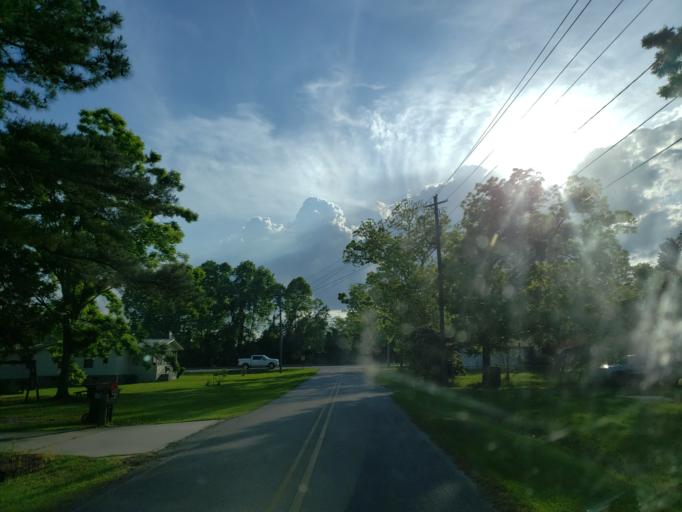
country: US
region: Georgia
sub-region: Lowndes County
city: Hahira
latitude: 31.0446
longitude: -83.3913
